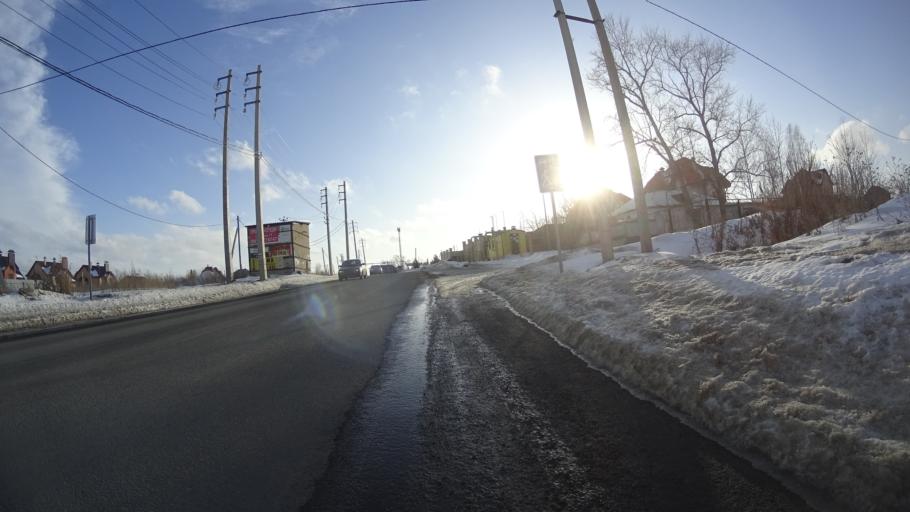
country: RU
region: Chelyabinsk
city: Sargazy
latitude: 55.1169
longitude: 61.2843
